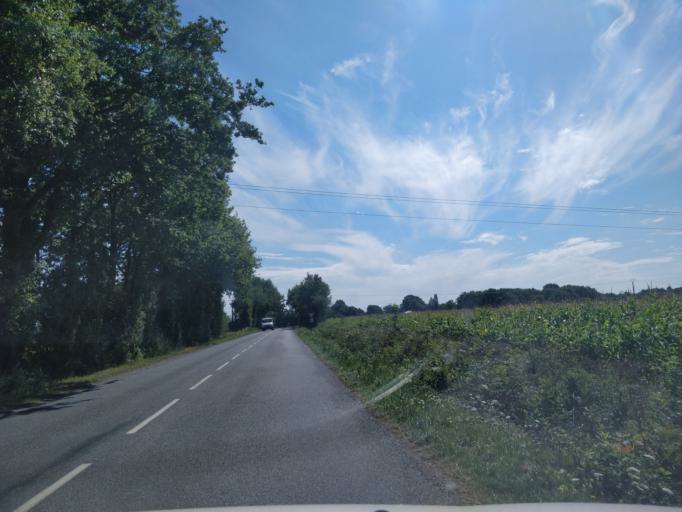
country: FR
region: Pays de la Loire
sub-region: Departement de la Loire-Atlantique
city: Derval
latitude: 47.6876
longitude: -1.6892
